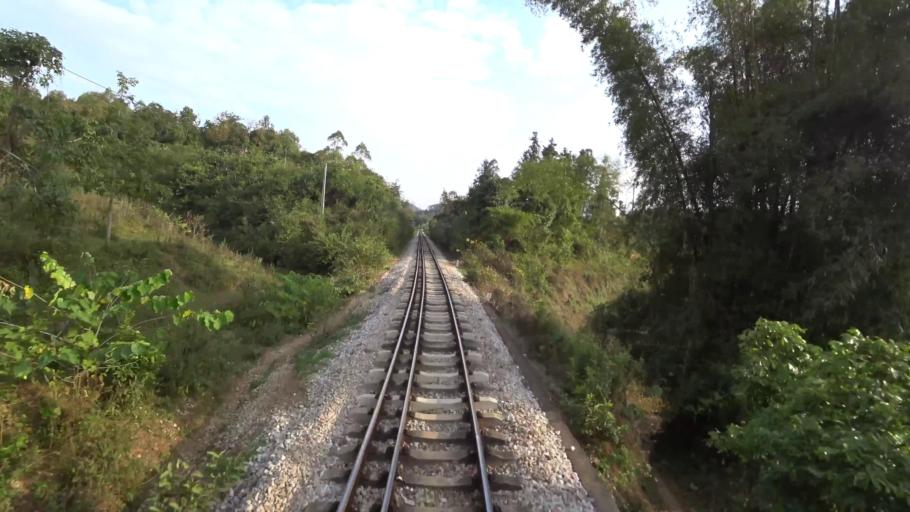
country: VN
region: Lang Son
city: Thi Tran Cao Loc
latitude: 21.9285
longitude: 106.7028
